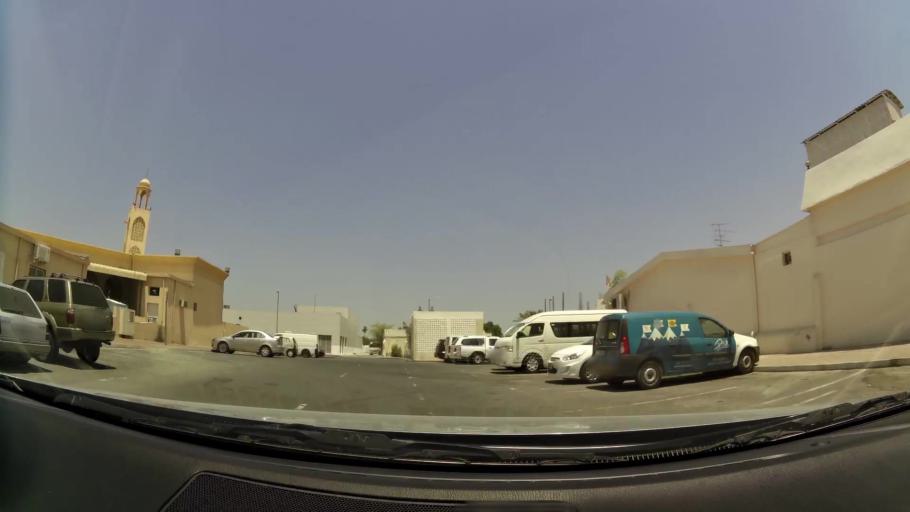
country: AE
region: Dubai
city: Dubai
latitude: 25.2038
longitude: 55.2531
